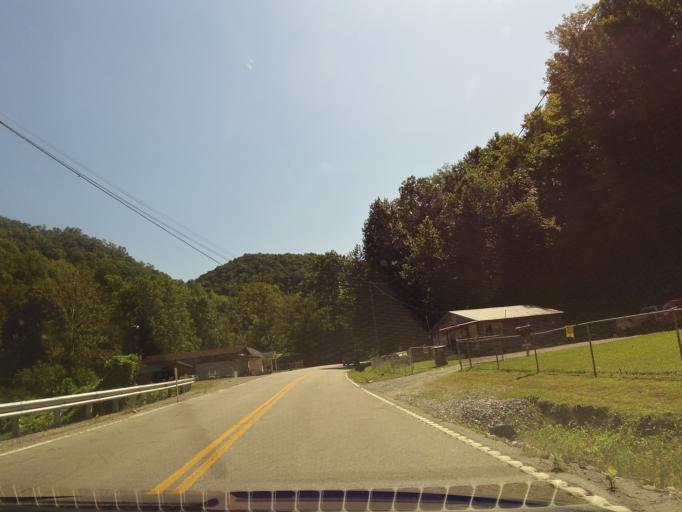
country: US
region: Kentucky
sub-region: Leslie County
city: Hyden
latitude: 37.1609
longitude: -83.5095
